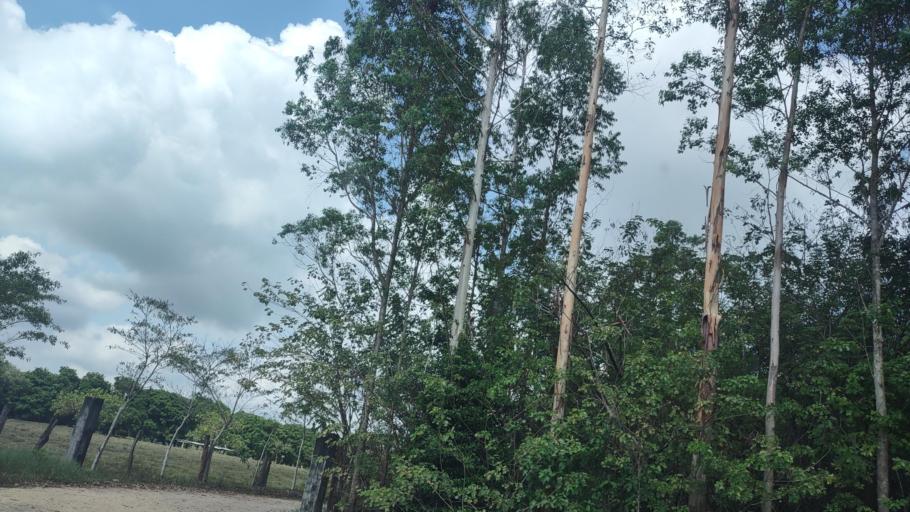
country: MX
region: Veracruz
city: Las Choapas
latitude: 17.9456
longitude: -94.0998
